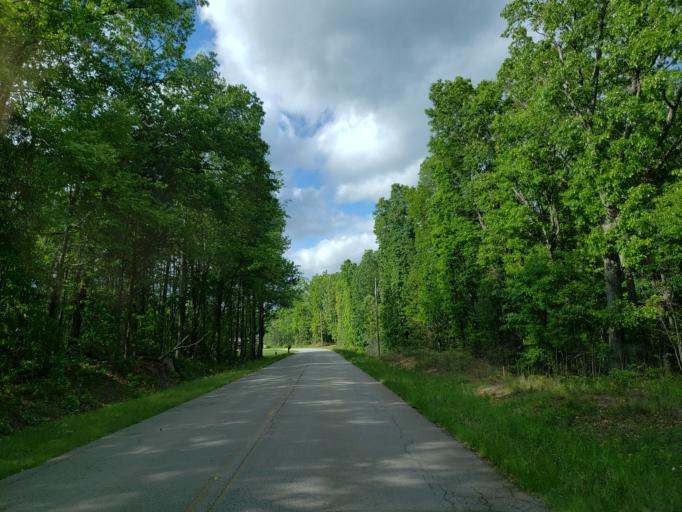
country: US
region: Georgia
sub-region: Carroll County
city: Mount Zion
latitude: 33.6407
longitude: -85.2783
